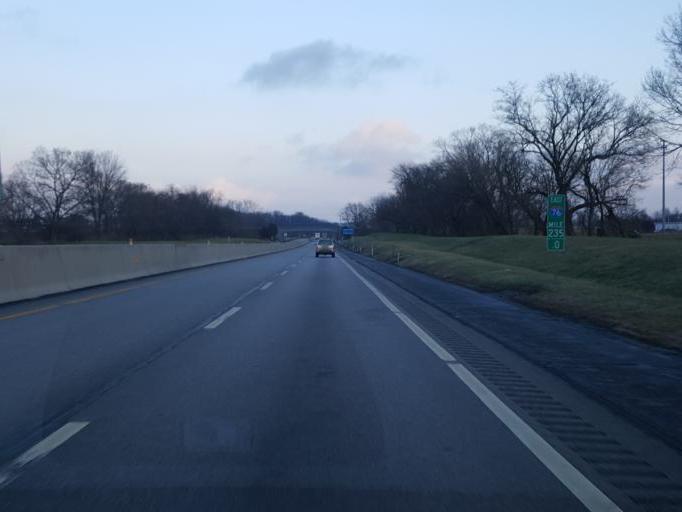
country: US
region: Pennsylvania
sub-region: Cumberland County
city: Mechanicsburg
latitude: 40.1966
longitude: -76.9997
